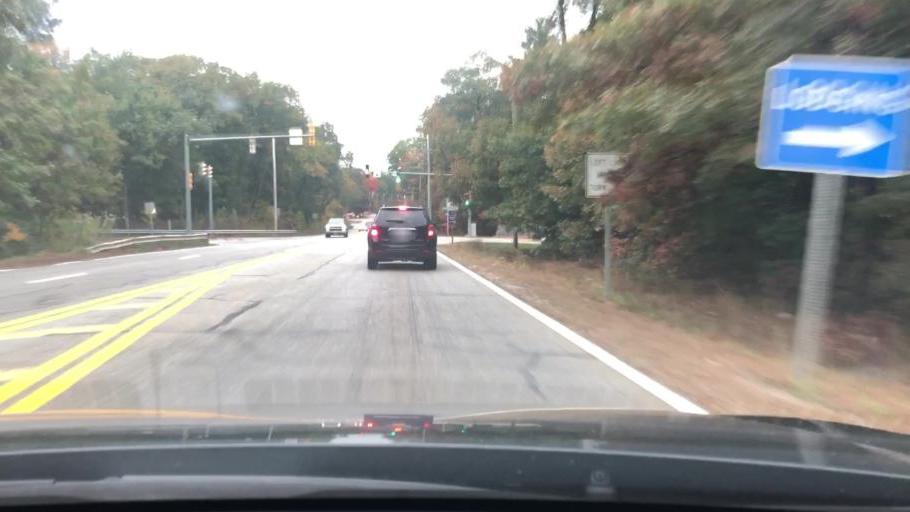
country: US
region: Massachusetts
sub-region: Middlesex County
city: Chelmsford
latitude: 42.6265
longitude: -71.3687
